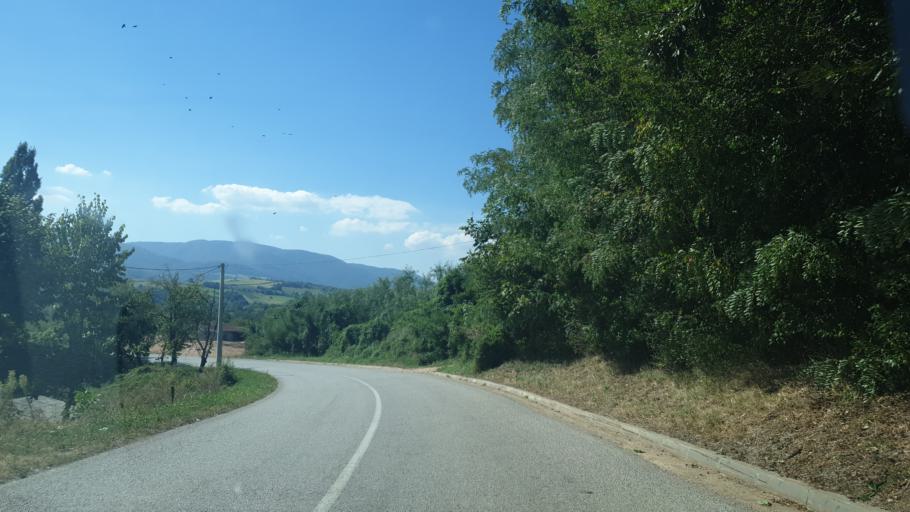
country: RS
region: Central Serbia
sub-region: Kolubarski Okrug
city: Mionica
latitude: 44.1932
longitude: 20.0728
